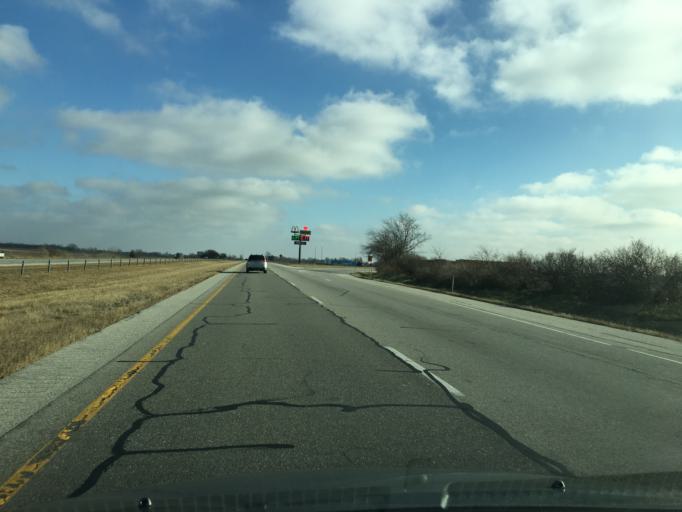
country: US
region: Indiana
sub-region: Decatur County
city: Saint Paul
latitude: 39.4533
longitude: -85.6295
